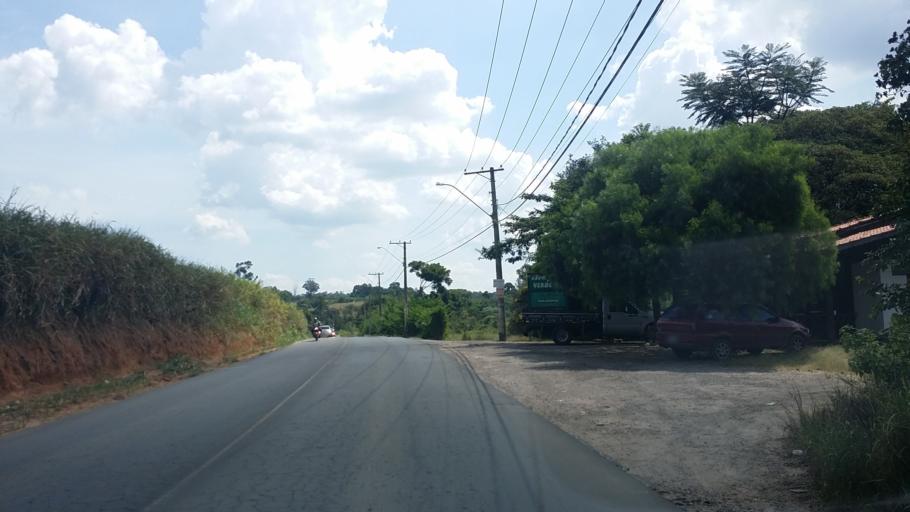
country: BR
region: Sao Paulo
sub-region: Itupeva
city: Itupeva
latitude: -23.1774
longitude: -47.0578
